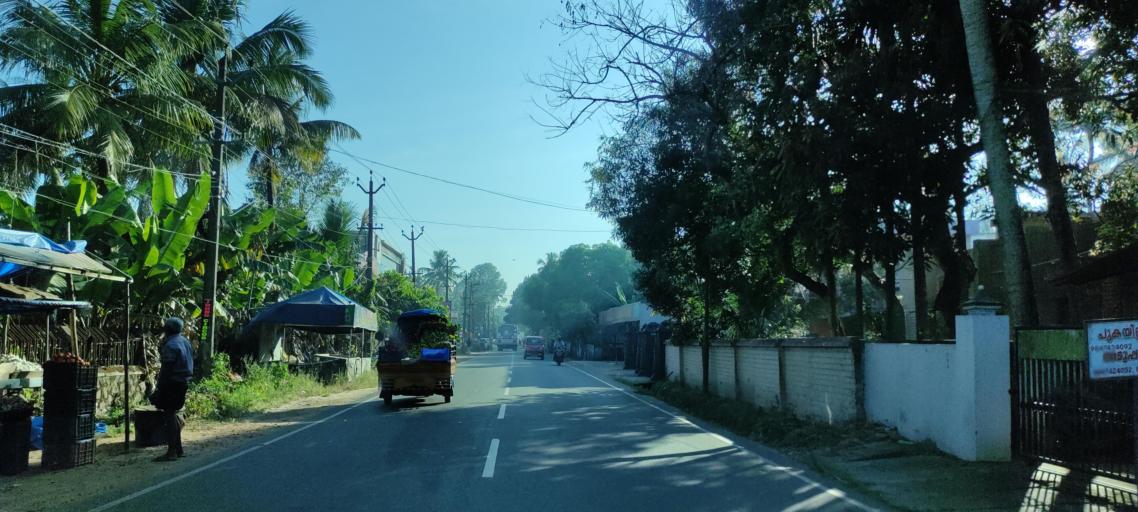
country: IN
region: Kerala
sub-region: Alappuzha
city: Kayankulam
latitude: 9.1763
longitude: 76.5189
